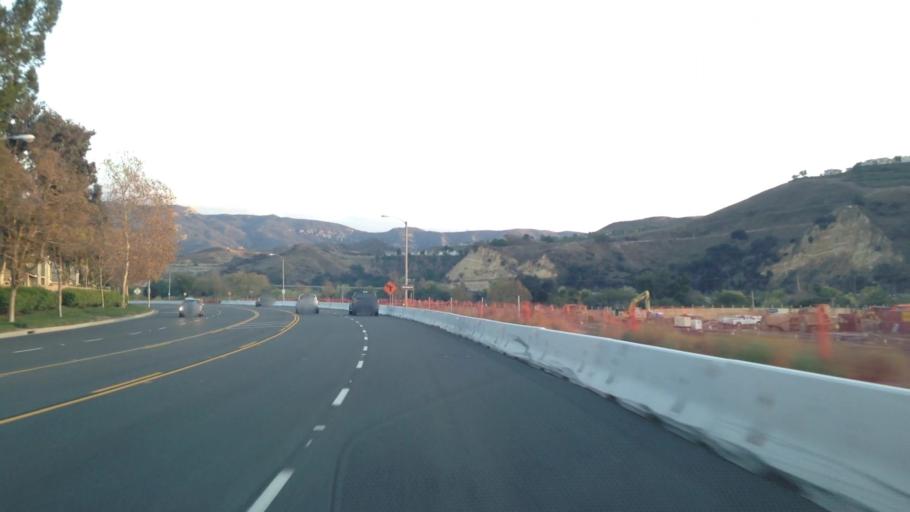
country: US
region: California
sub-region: Orange County
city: Yorba Linda
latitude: 33.8731
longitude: -117.7289
